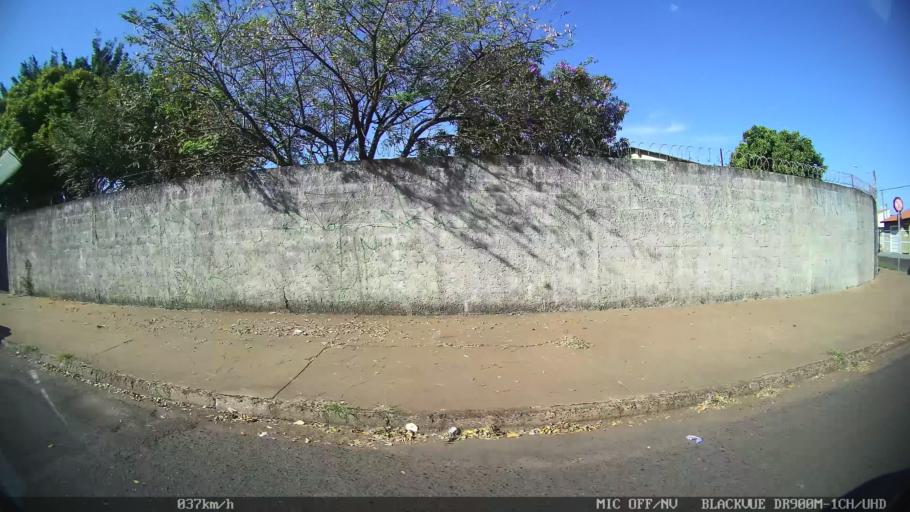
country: BR
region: Sao Paulo
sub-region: Franca
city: Franca
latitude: -20.4898
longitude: -47.4128
